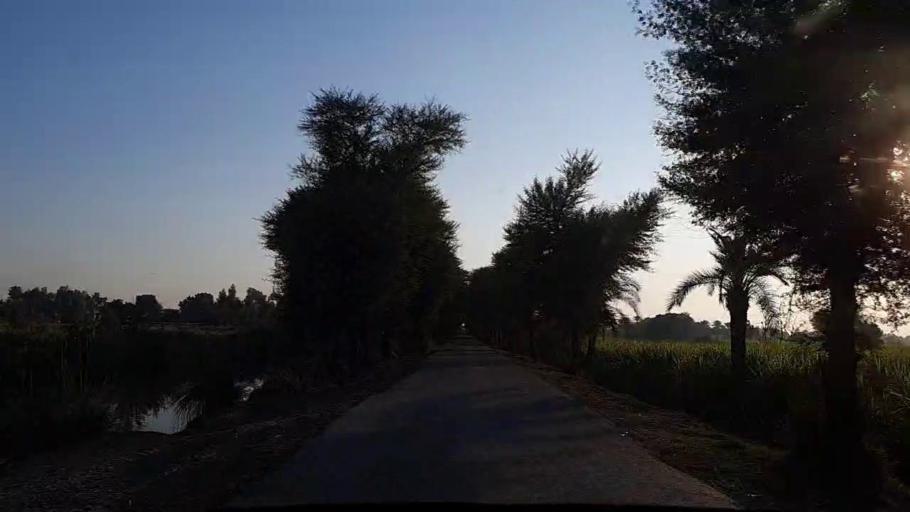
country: PK
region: Sindh
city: Sobhadero
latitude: 27.3914
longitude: 68.3846
